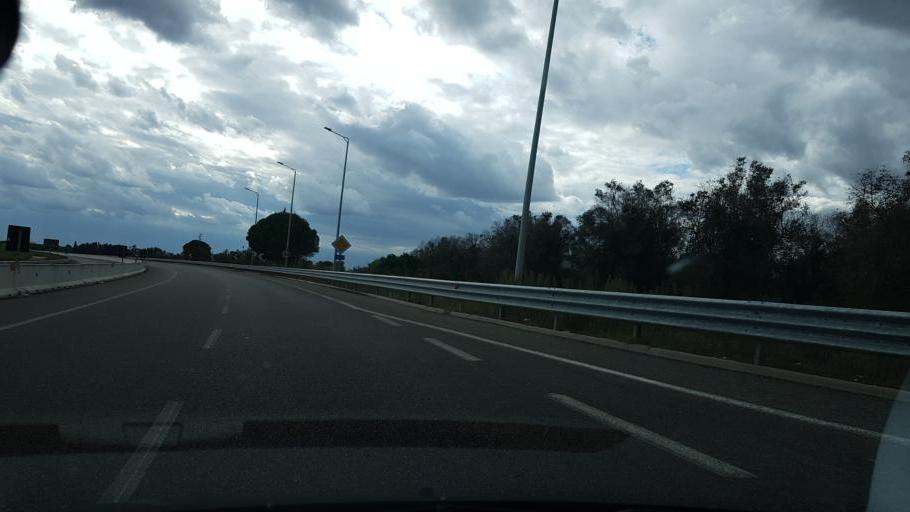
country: IT
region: Apulia
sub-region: Provincia di Lecce
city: Palmariggi
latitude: 40.1333
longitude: 18.3935
